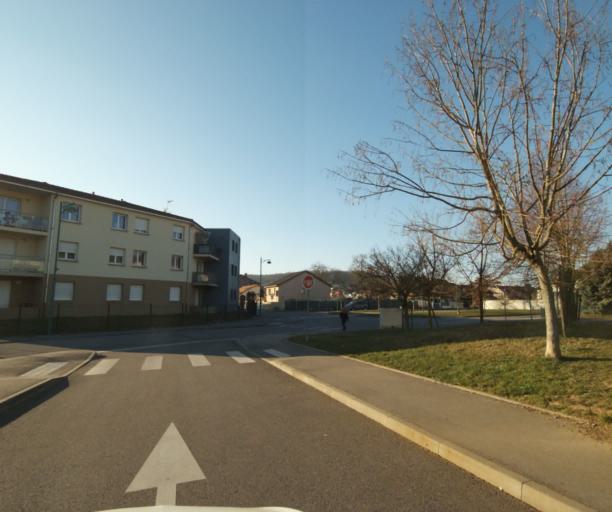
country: FR
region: Lorraine
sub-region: Departement de Meurthe-et-Moselle
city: Malzeville
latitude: 48.7139
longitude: 6.1814
